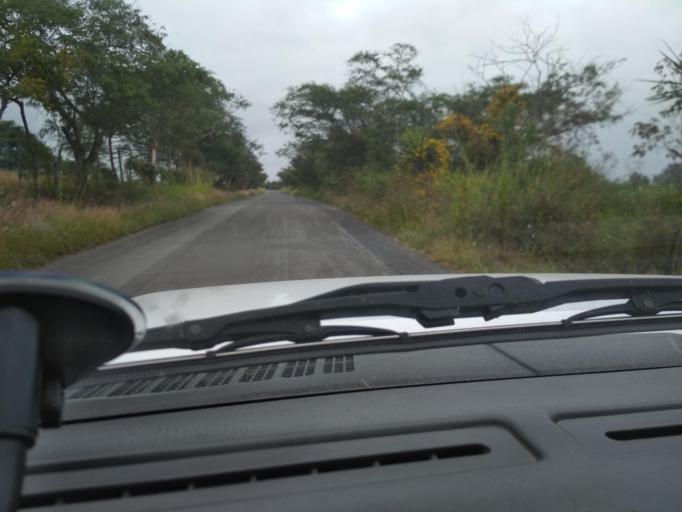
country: MX
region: Veracruz
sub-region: Emiliano Zapata
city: Dos Rios
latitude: 19.5320
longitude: -96.7991
